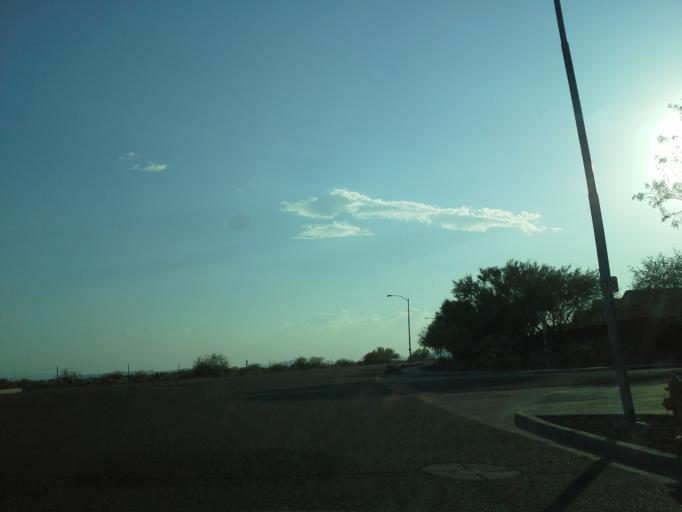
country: US
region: Arizona
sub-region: Maricopa County
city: Anthem
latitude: 33.8641
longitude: -112.1546
